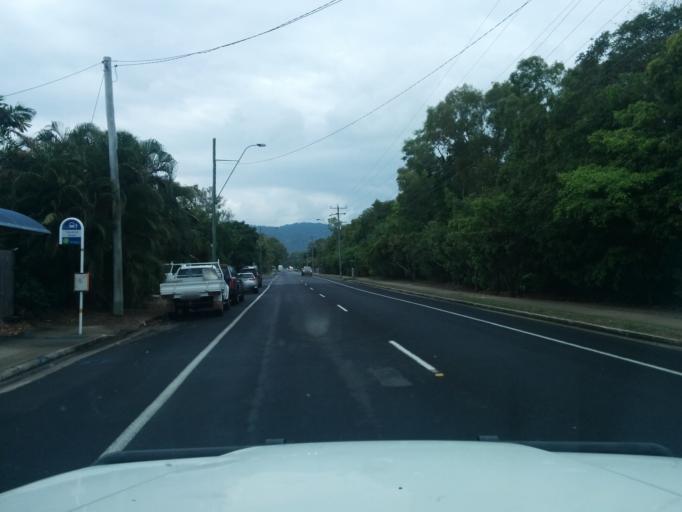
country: AU
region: Queensland
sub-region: Cairns
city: Yorkeys Knob
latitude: -16.8434
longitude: 145.7394
